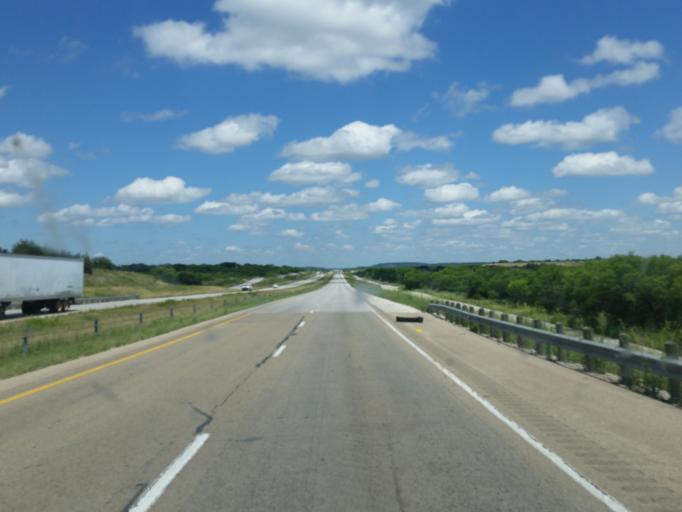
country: US
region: Texas
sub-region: Callahan County
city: Baird
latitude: 32.3847
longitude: -99.2899
